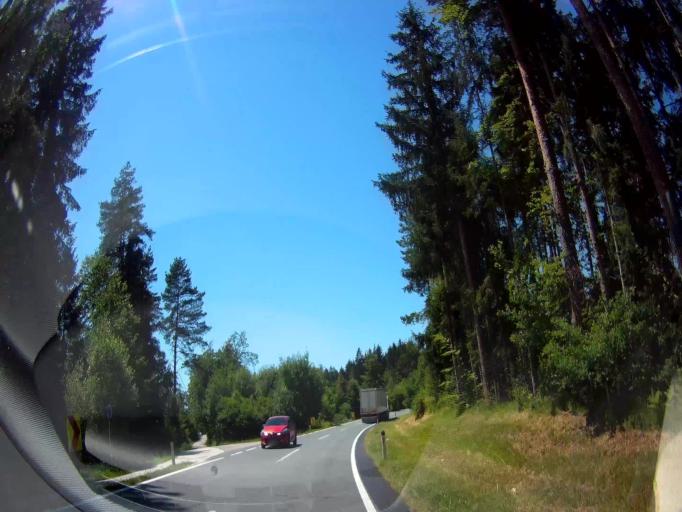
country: AT
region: Carinthia
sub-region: Politischer Bezirk Volkermarkt
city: Eberndorf
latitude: 46.6215
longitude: 14.6475
